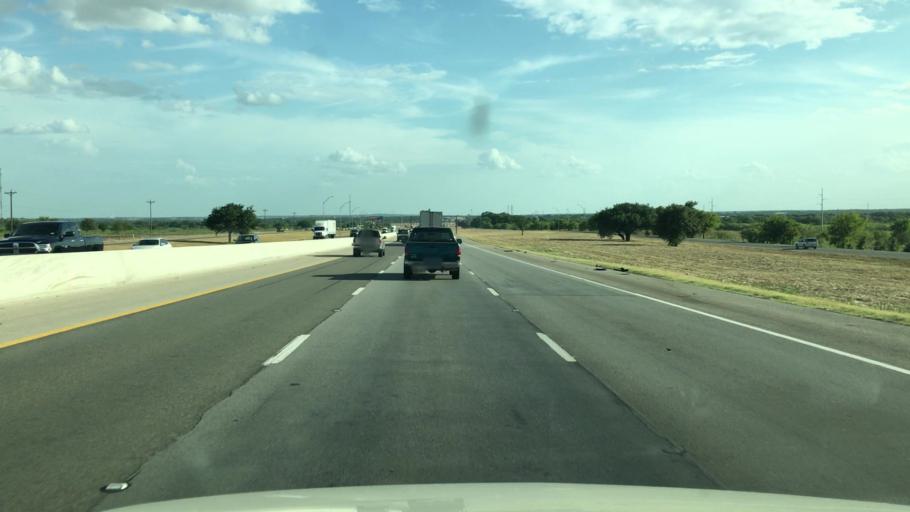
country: US
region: Texas
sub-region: Williamson County
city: Serenada
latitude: 30.7214
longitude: -97.6451
